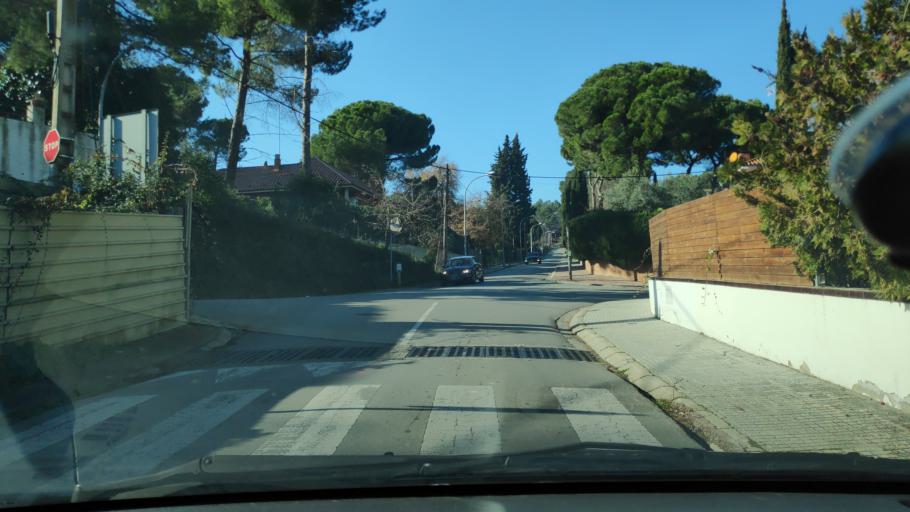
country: ES
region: Catalonia
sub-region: Provincia de Barcelona
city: Sant Quirze del Valles
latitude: 41.5062
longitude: 2.0837
